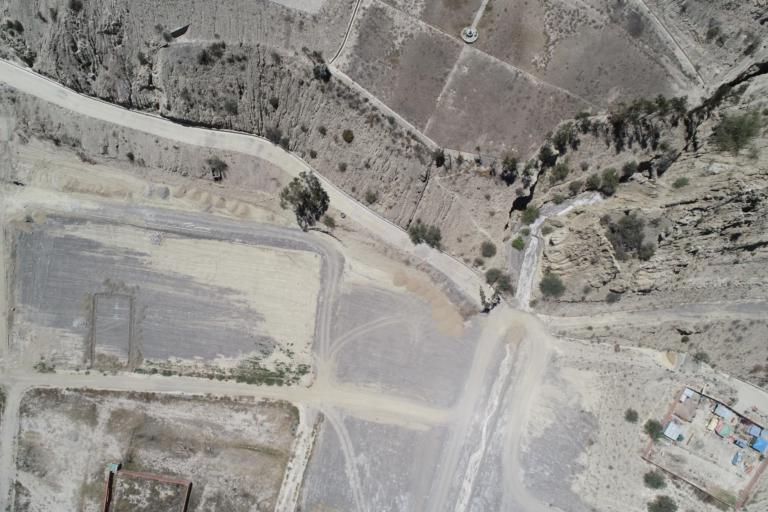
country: BO
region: La Paz
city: La Paz
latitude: -16.6187
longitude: -68.0604
